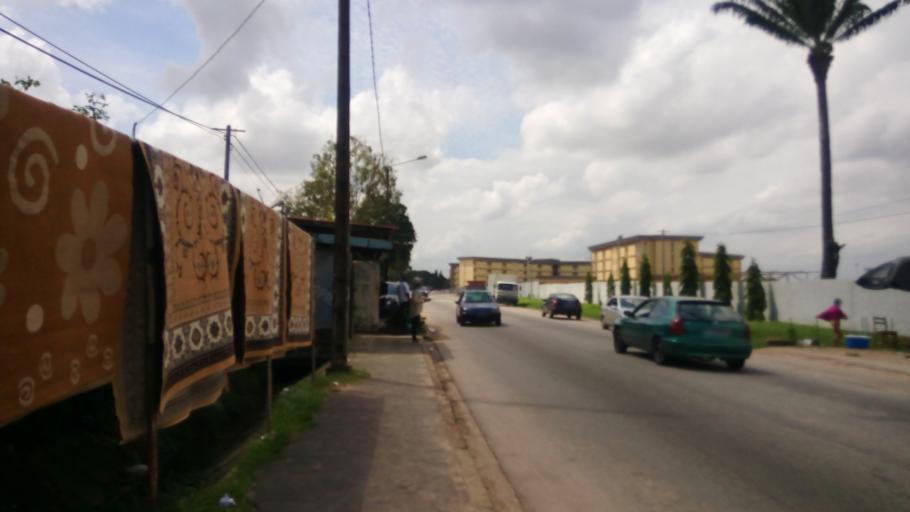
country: CI
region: Lagunes
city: Abidjan
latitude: 5.3359
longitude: -3.9964
